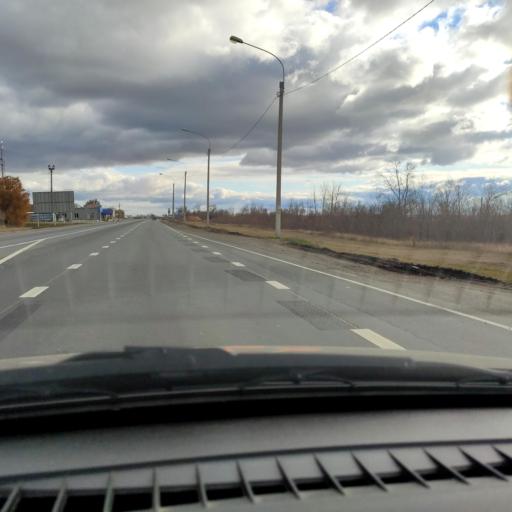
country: RU
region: Samara
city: Syzran'
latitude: 53.2097
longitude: 48.5100
